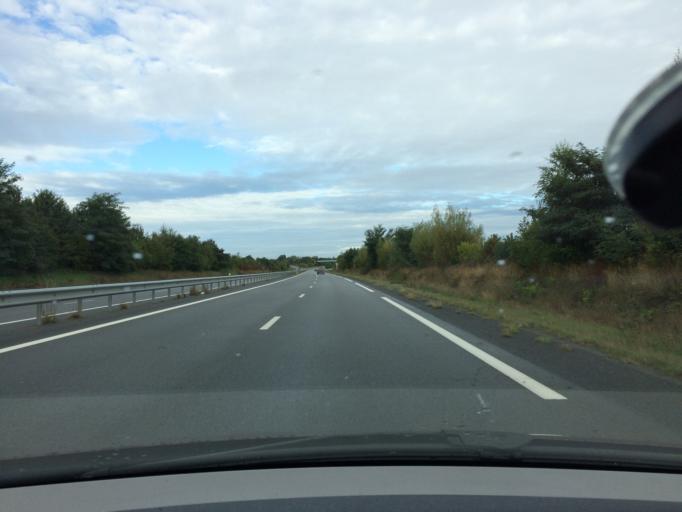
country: FR
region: Brittany
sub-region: Departement d'Ille-et-Vilaine
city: Corps-Nuds
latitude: 47.9766
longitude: -1.5513
